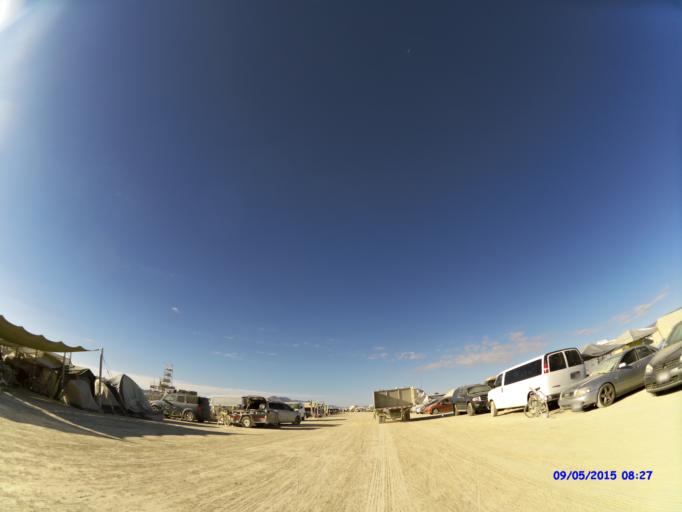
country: US
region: Nevada
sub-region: Pershing County
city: Lovelock
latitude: 40.7902
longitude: -119.2168
